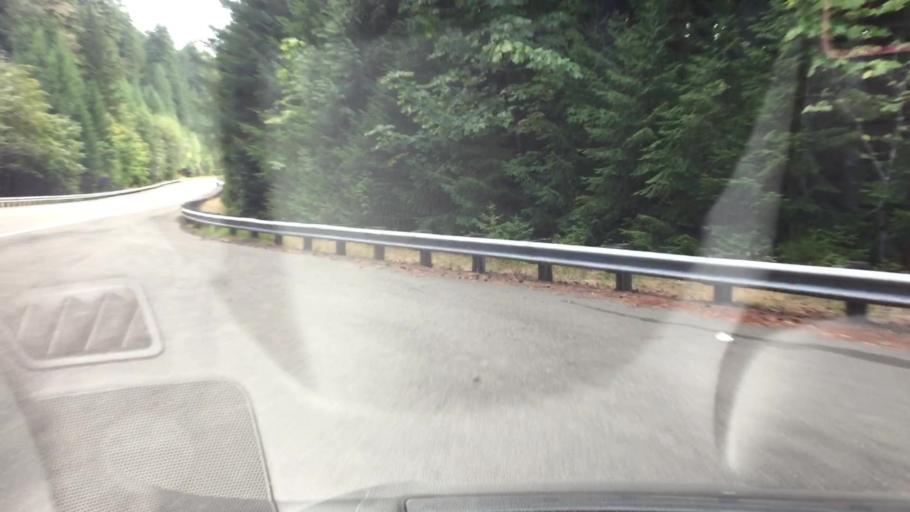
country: US
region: Washington
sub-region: Pierce County
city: Buckley
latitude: 46.6539
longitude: -121.6039
